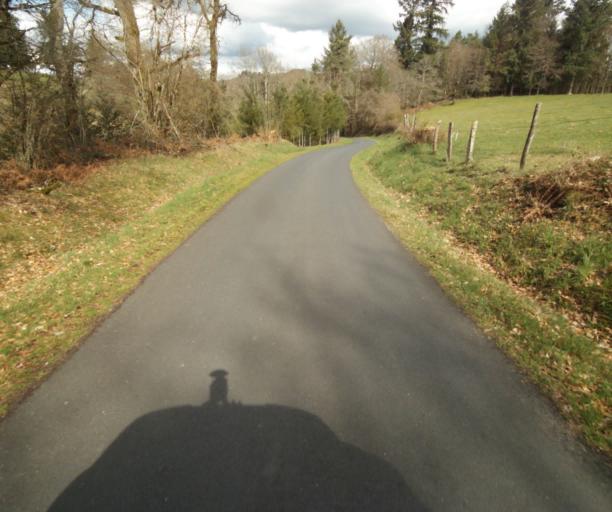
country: FR
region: Limousin
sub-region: Departement de la Correze
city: Correze
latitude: 45.3697
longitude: 1.8875
